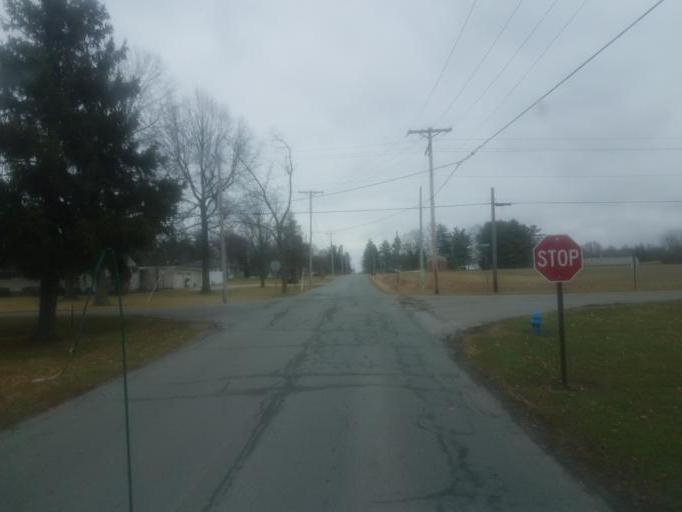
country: US
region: Ohio
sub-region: Crawford County
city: Galion
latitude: 40.7557
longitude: -82.7834
